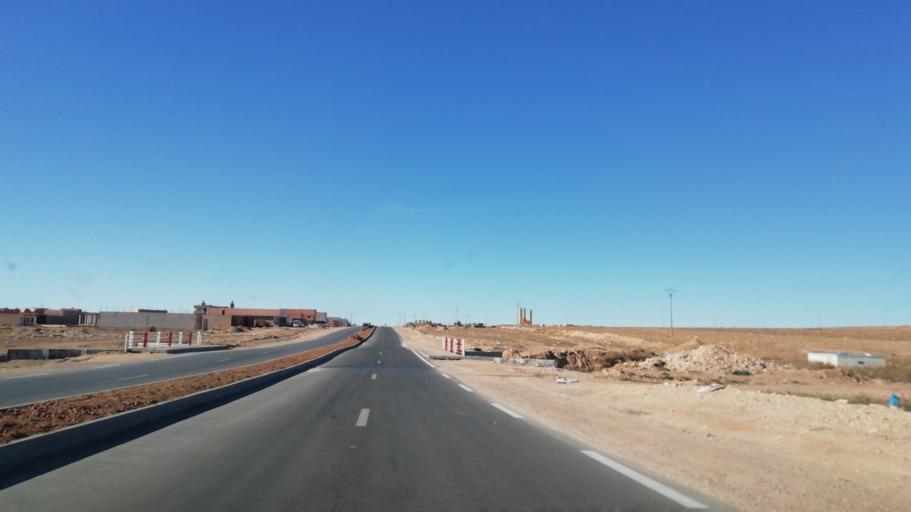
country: DZ
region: Tlemcen
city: Sebdou
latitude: 34.2151
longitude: -1.2445
